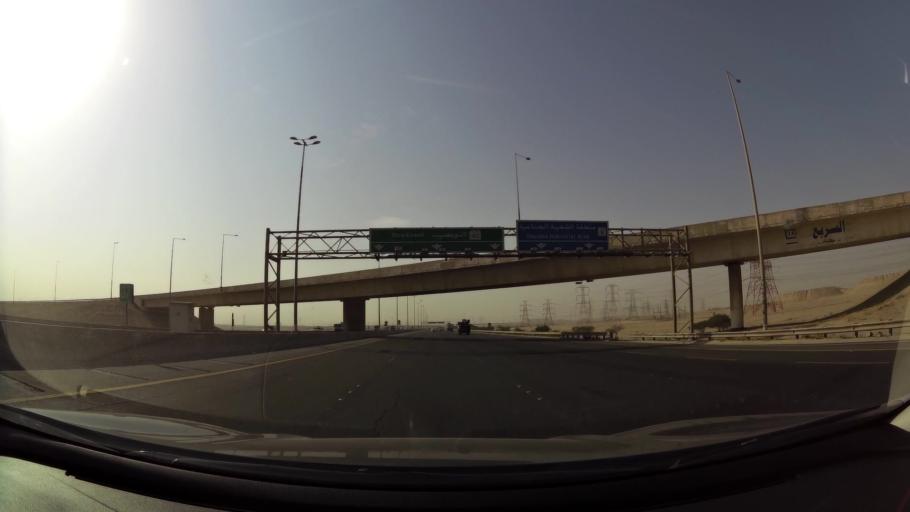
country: KW
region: Al Ahmadi
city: Al Ahmadi
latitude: 29.0481
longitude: 48.0949
